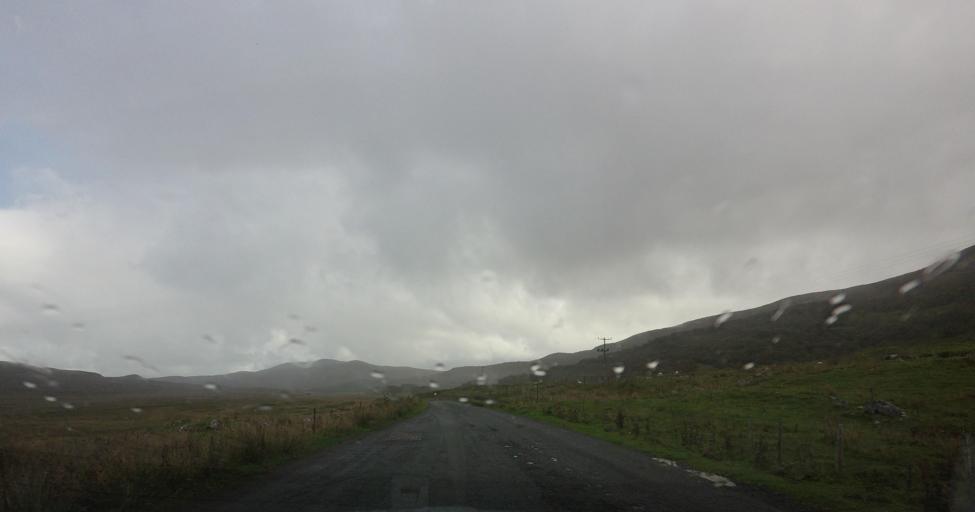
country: GB
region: Scotland
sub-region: Highland
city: Portree
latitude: 57.2076
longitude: -5.9831
